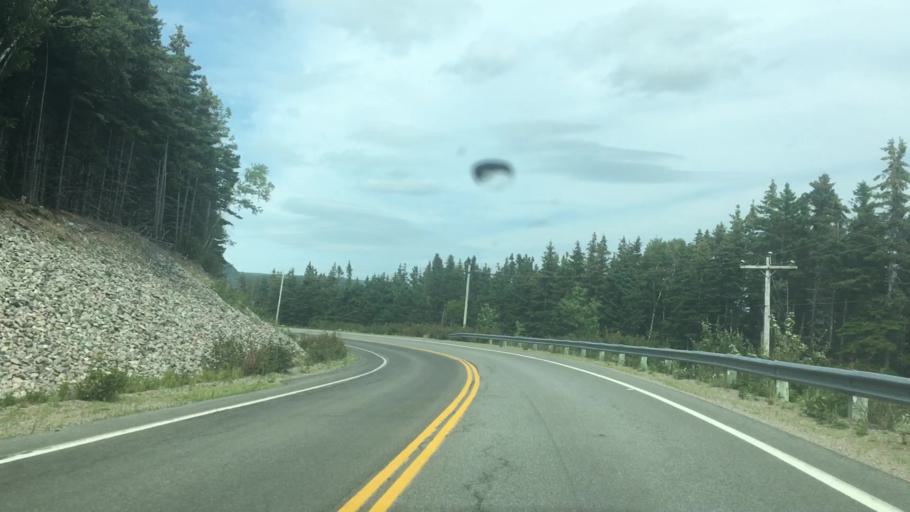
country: CA
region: Nova Scotia
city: Sydney Mines
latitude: 46.5367
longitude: -60.4136
